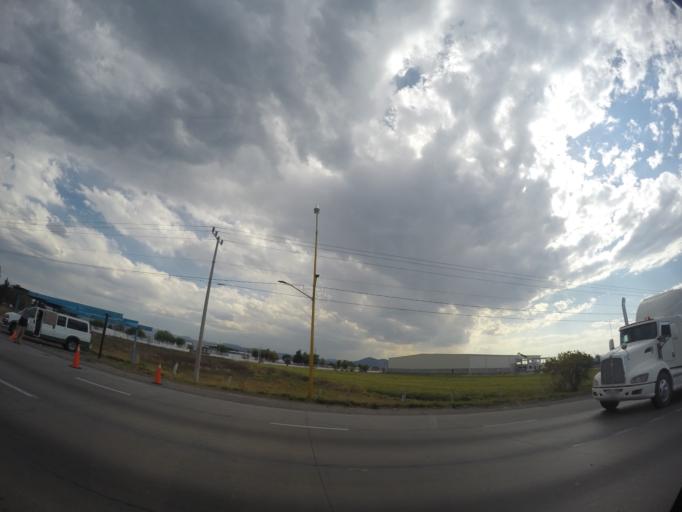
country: MX
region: Queretaro
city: La Estancia
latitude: 20.4319
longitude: -100.0630
